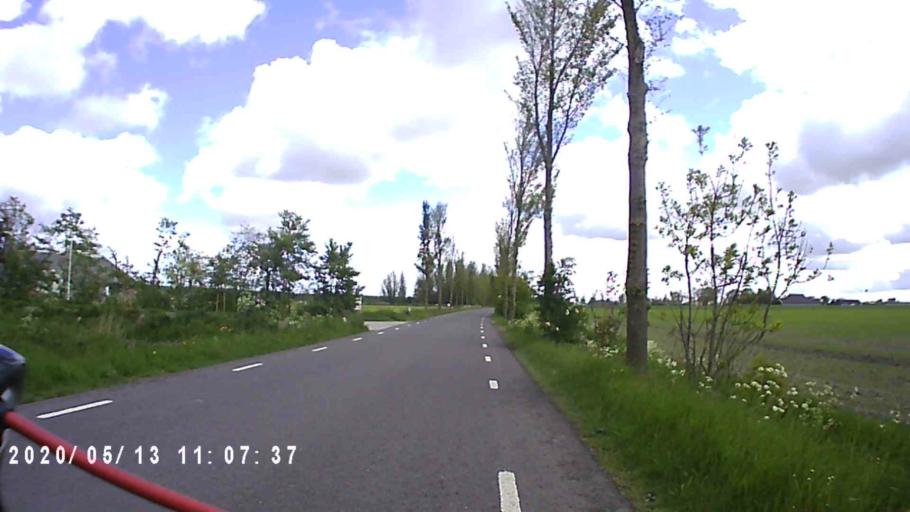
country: NL
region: Groningen
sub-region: Gemeente Zuidhorn
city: Grijpskerk
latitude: 53.2919
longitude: 6.3349
